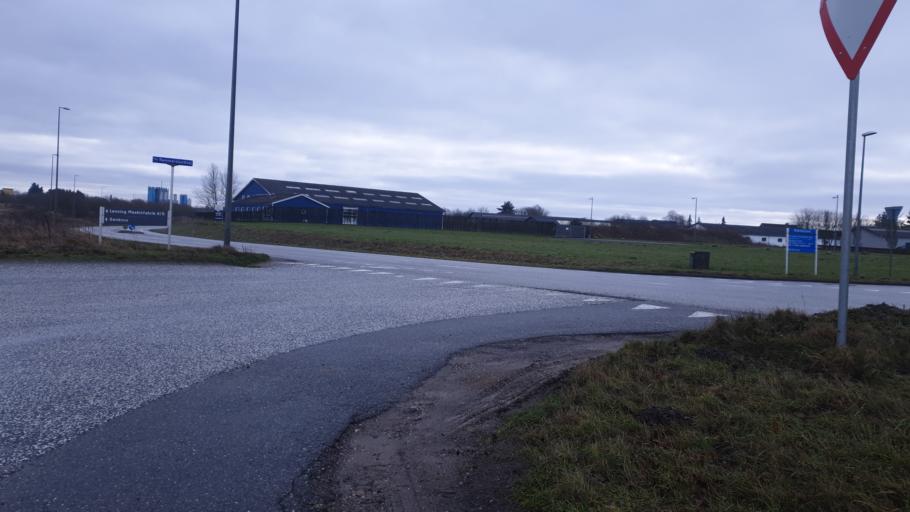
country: DK
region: Central Jutland
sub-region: Hedensted Kommune
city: Hedensted
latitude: 55.7811
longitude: 9.7032
